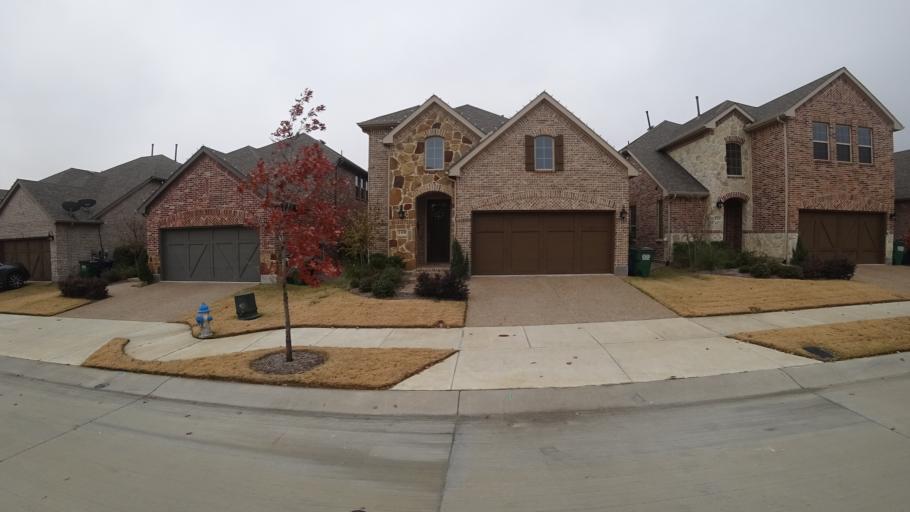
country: US
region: Texas
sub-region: Denton County
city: The Colony
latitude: 33.0577
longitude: -96.9020
